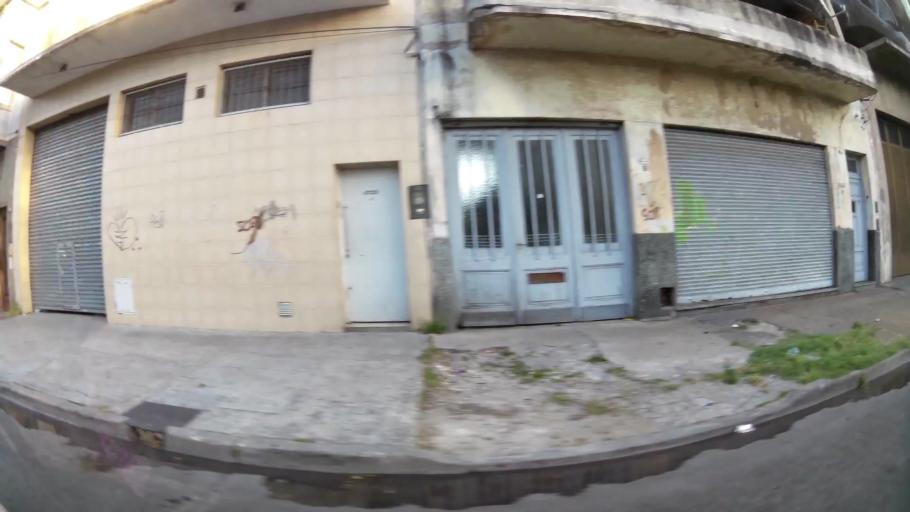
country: AR
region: Buenos Aires
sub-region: Partido de General San Martin
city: General San Martin
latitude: -34.5527
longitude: -58.5146
